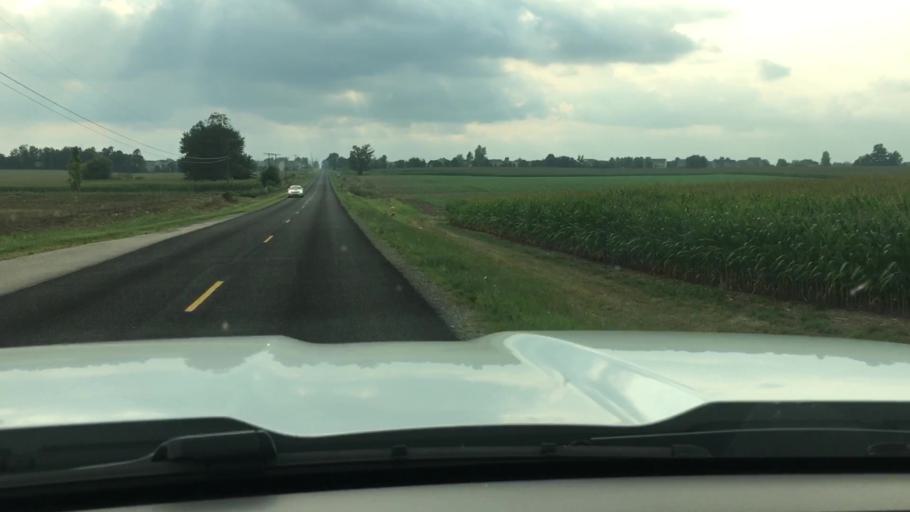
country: US
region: Michigan
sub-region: Ottawa County
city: Hudsonville
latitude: 42.8330
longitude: -85.8442
